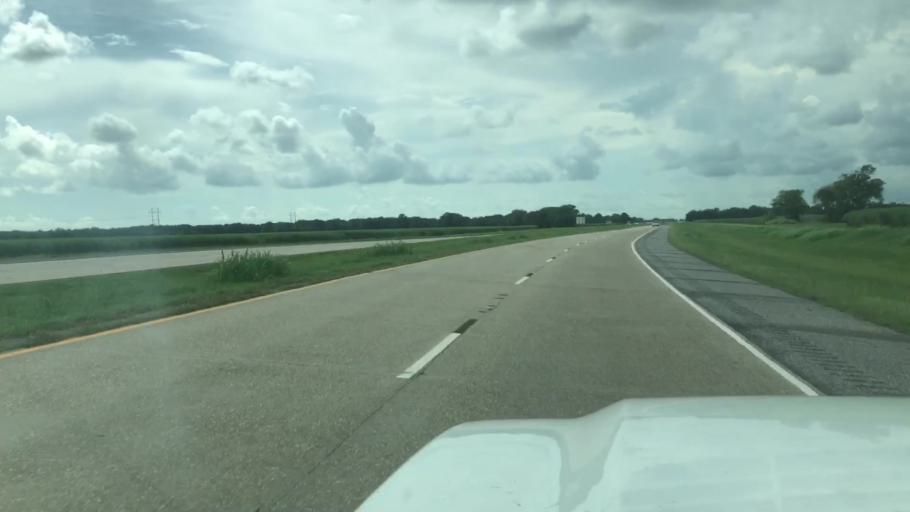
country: US
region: Louisiana
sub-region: Saint Mary Parish
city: Franklin
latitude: 29.7583
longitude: -91.4736
